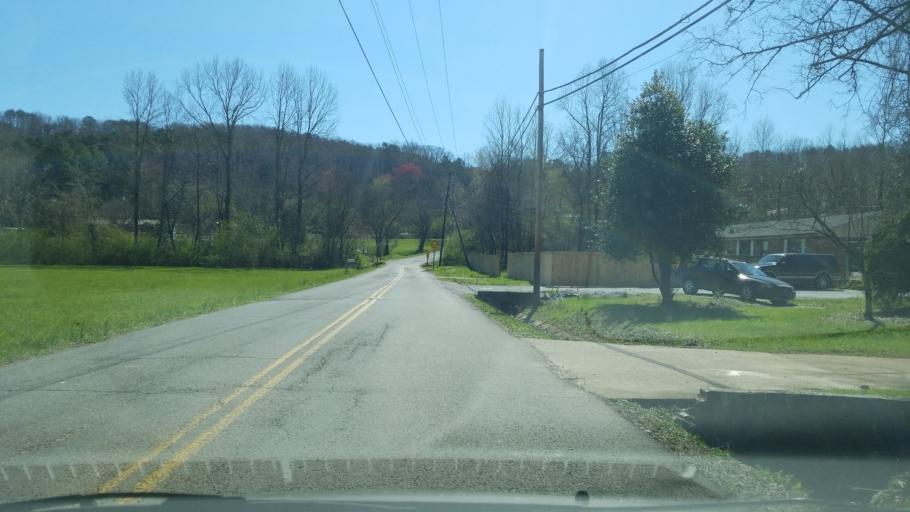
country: US
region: Tennessee
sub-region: Hamilton County
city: Falling Water
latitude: 35.1712
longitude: -85.2582
